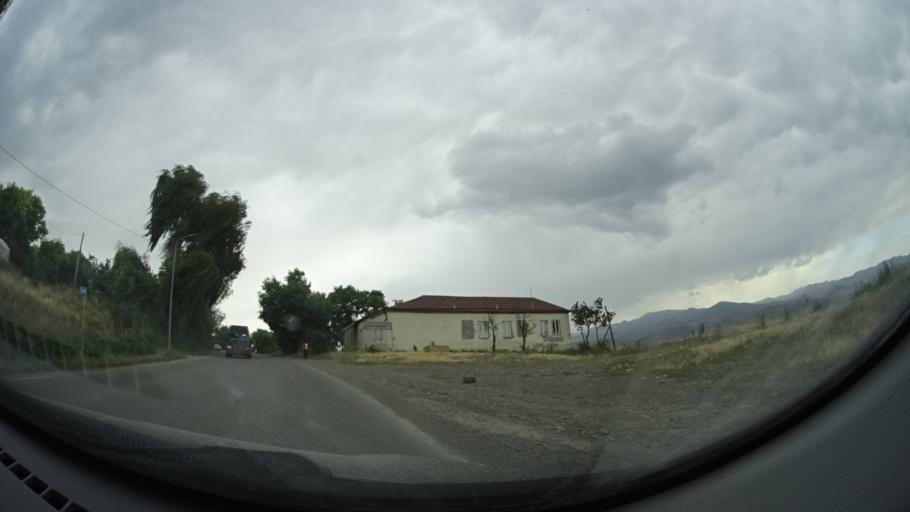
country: GE
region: Samtskhe-Javakheti
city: Akhaltsikhe
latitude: 41.6352
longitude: 43.0423
